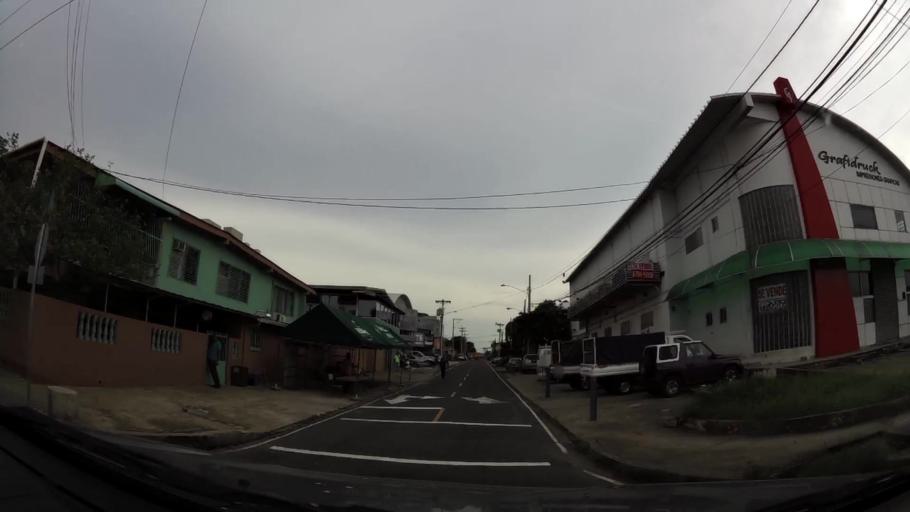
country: PA
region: Panama
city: San Miguelito
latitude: 9.0182
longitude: -79.4878
